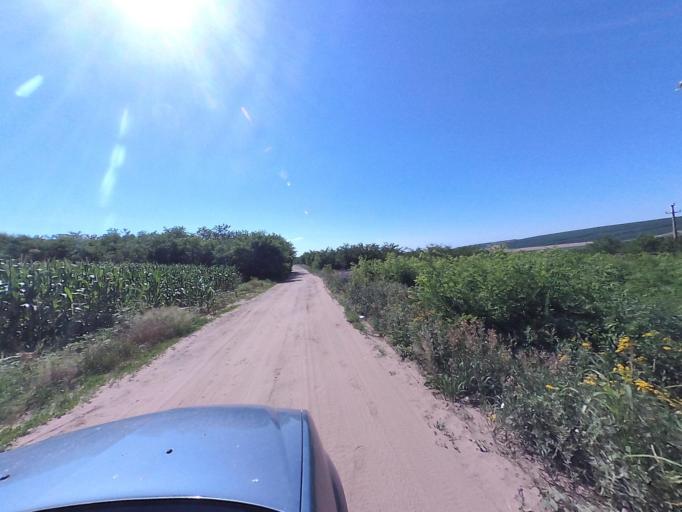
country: RO
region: Vaslui
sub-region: Comuna Costesti
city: Costesti
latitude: 46.4850
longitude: 27.7708
